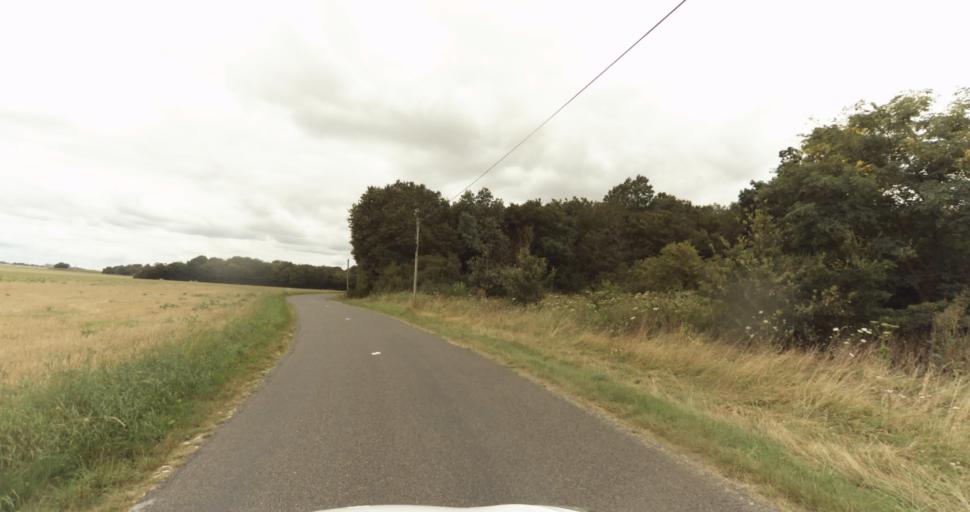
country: FR
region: Centre
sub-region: Departement d'Eure-et-Loir
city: Saint-Lubin-des-Joncherets
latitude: 48.8230
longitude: 1.2337
